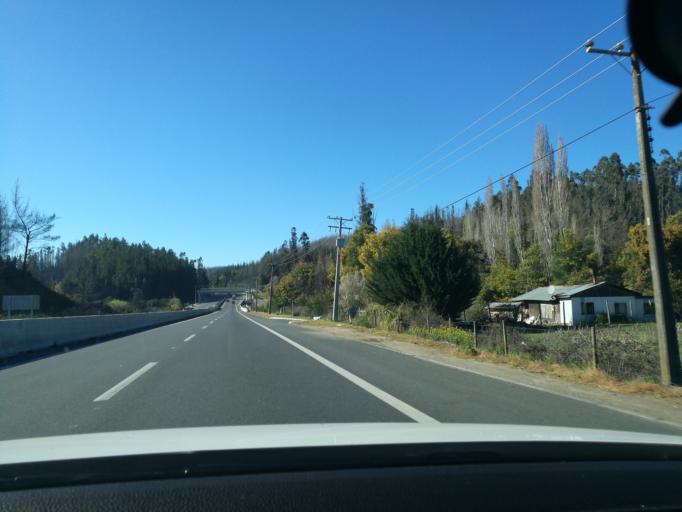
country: CL
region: Biobio
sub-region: Provincia de Concepcion
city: Penco
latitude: -36.8512
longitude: -72.9010
